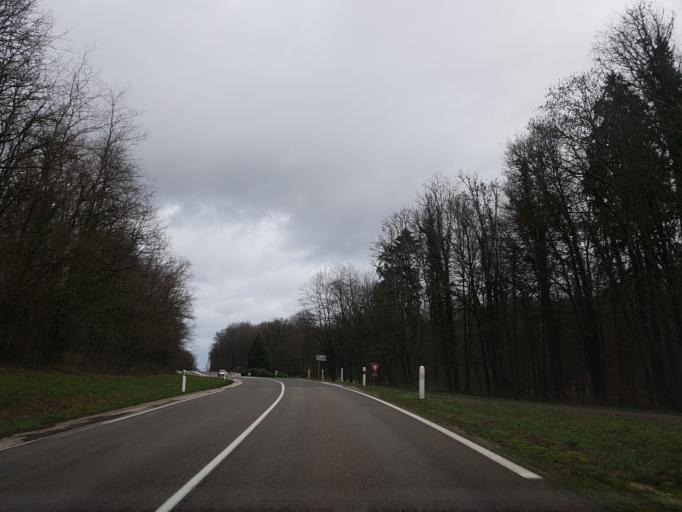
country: FR
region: Franche-Comte
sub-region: Departement de la Haute-Saone
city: Scey-sur-Saone-et-Saint-Albin
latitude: 47.6883
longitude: 6.0011
